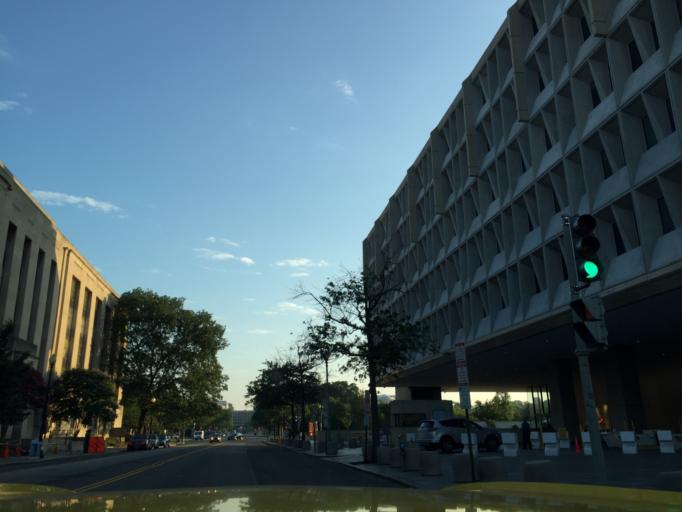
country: US
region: Washington, D.C.
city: Washington, D.C.
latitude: 38.8862
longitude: -77.0152
